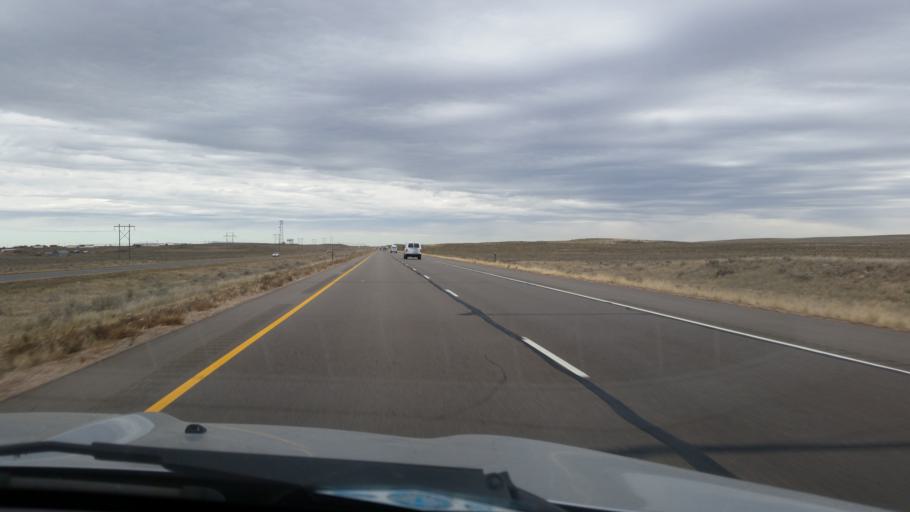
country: US
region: Colorado
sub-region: Morgan County
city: Brush
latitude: 40.3249
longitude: -103.4867
